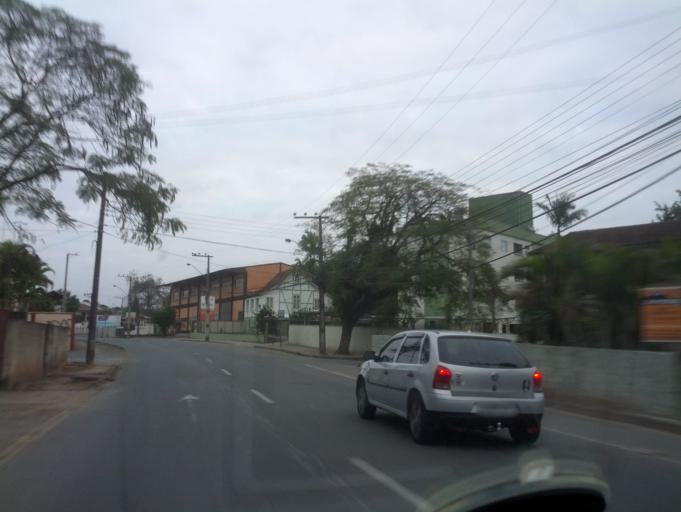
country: BR
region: Santa Catarina
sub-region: Blumenau
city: Blumenau
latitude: -26.8714
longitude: -49.0862
